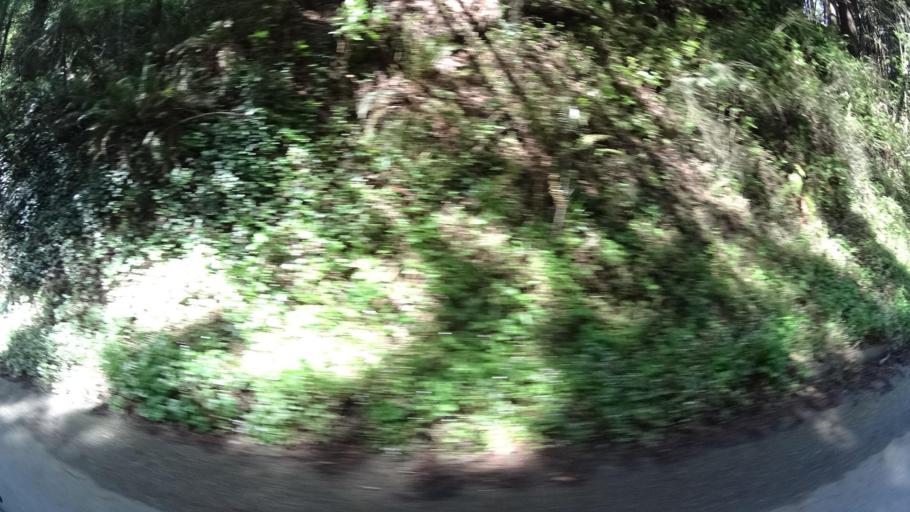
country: US
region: California
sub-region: Humboldt County
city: Hydesville
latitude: 40.5693
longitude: -124.1129
